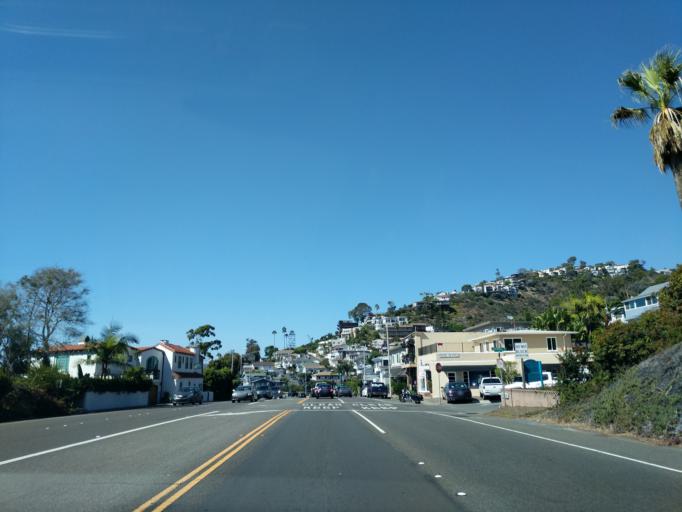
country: US
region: California
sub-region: Orange County
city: Laguna Beach
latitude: 33.5199
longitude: -117.7607
